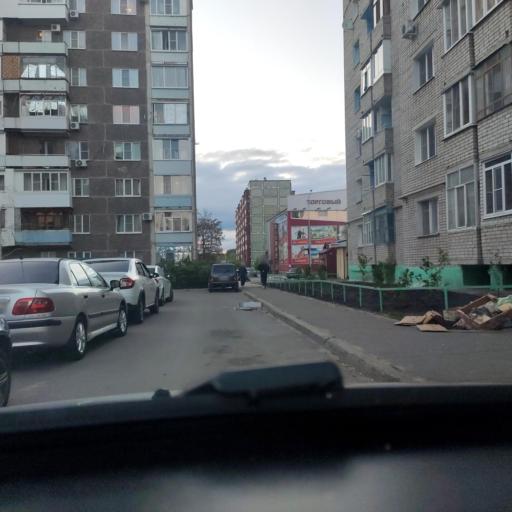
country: RU
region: Voronezj
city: Novovoronezh
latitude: 51.3187
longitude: 39.2048
